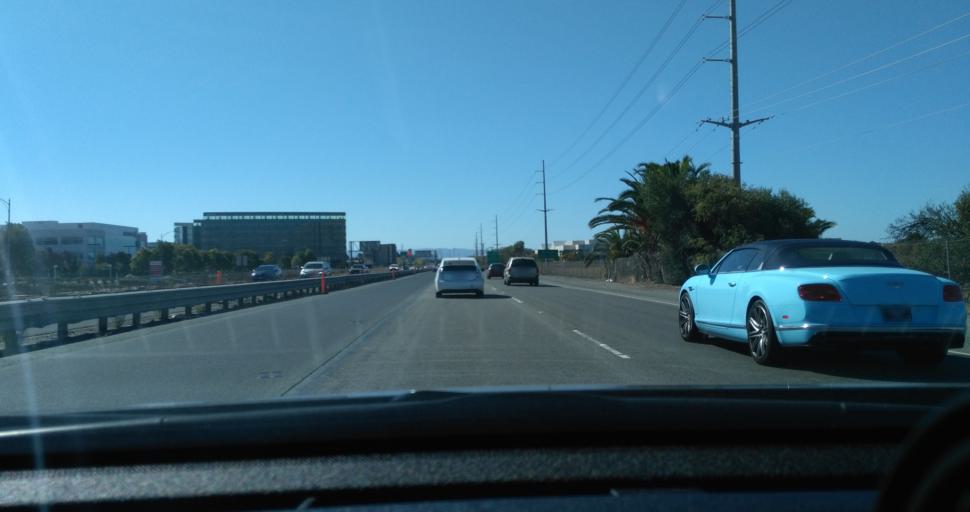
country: US
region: California
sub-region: Santa Clara County
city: Milpitas
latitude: 37.4195
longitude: -121.9467
